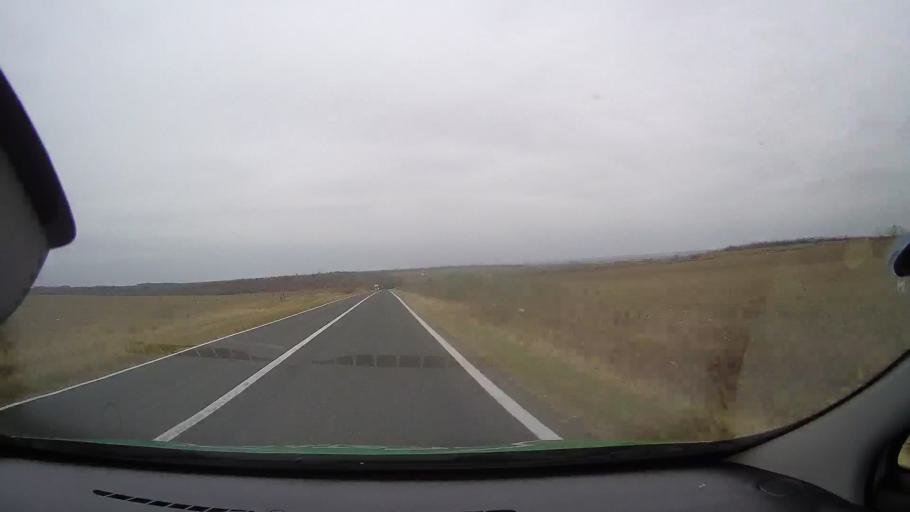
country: RO
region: Constanta
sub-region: Comuna Garliciu
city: Garliciu
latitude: 44.7106
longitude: 28.0820
